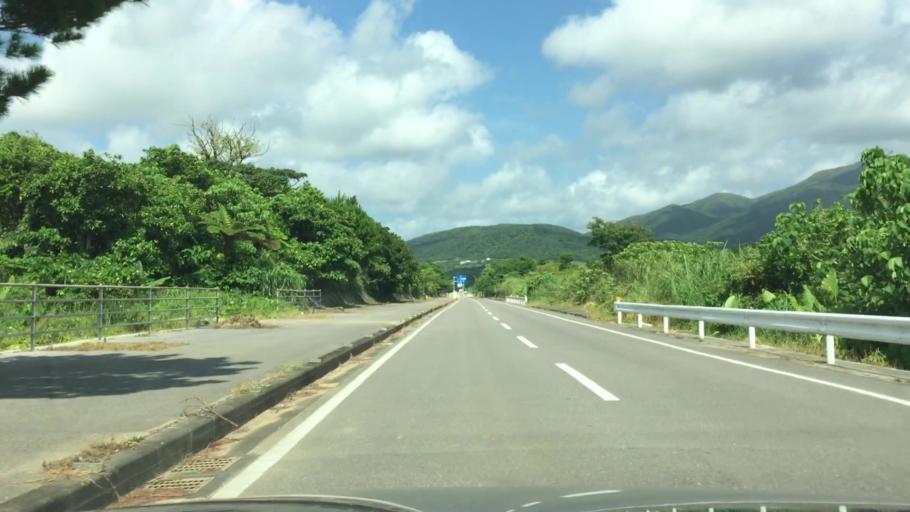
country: JP
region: Okinawa
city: Ishigaki
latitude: 24.4104
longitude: 124.2200
